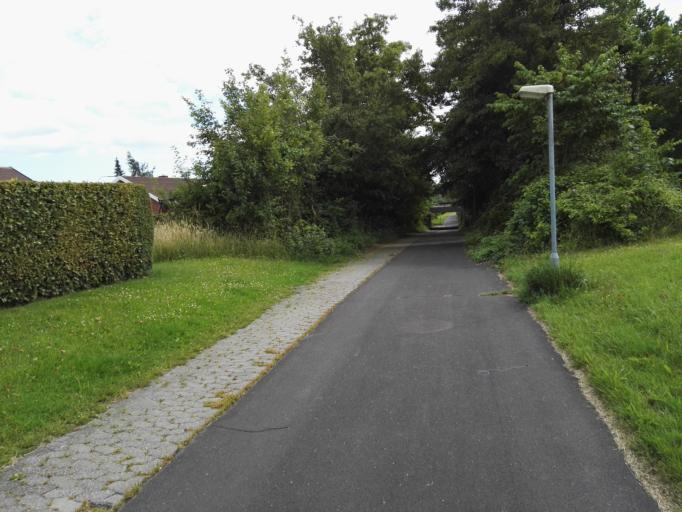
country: DK
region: Capital Region
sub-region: Ballerup Kommune
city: Malov
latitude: 55.7556
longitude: 12.3300
